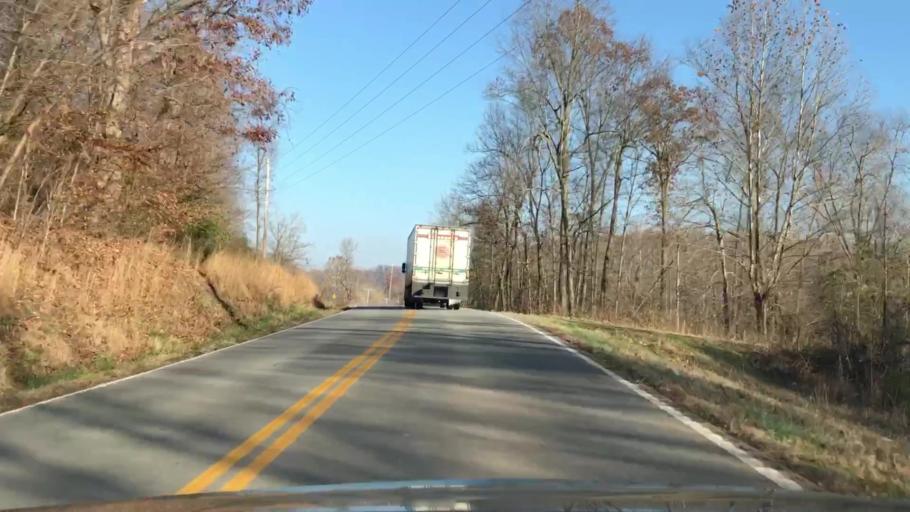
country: US
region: Kentucky
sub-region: Grayson County
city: Leitchfield
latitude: 37.4237
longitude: -86.2785
